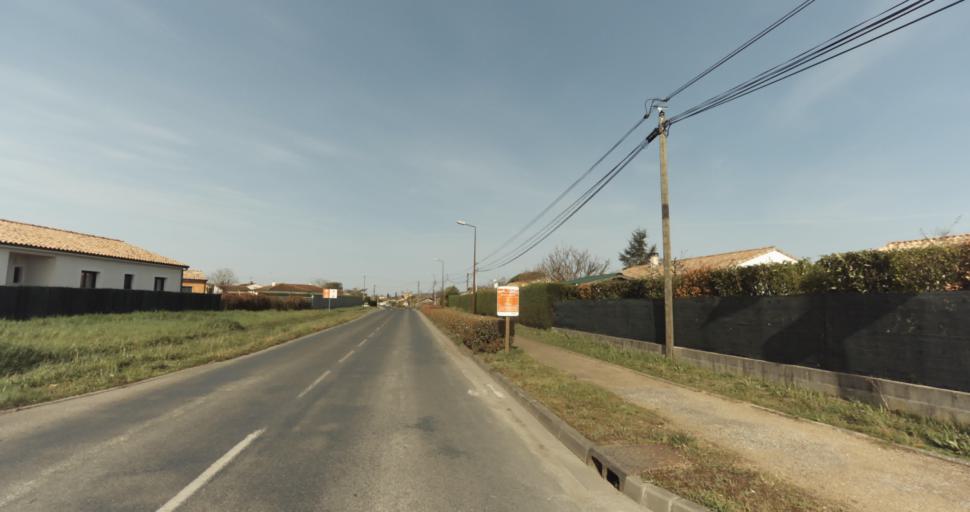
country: FR
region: Midi-Pyrenees
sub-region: Departement du Tarn
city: Saint-Sulpice-la-Pointe
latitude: 43.7716
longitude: 1.6995
